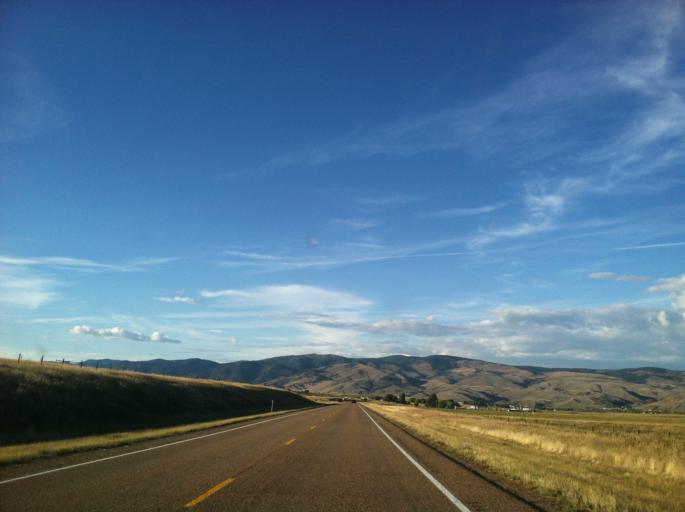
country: US
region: Montana
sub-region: Granite County
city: Philipsburg
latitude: 46.6271
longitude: -113.1702
